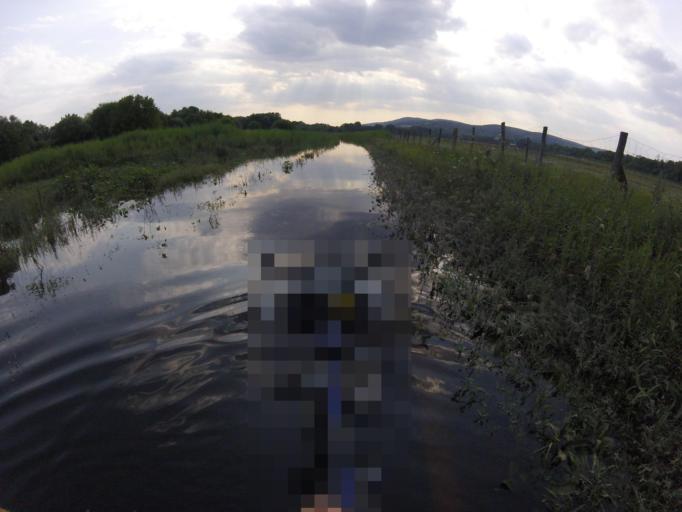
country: HU
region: Pest
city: Szob
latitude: 47.8307
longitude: 18.8486
